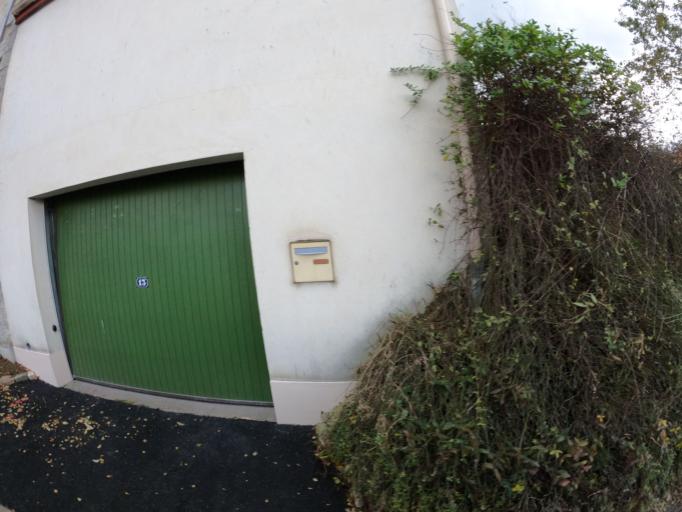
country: FR
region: Ile-de-France
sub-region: Departement de Seine-et-Marne
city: Coupvray
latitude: 48.8942
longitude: 2.7938
